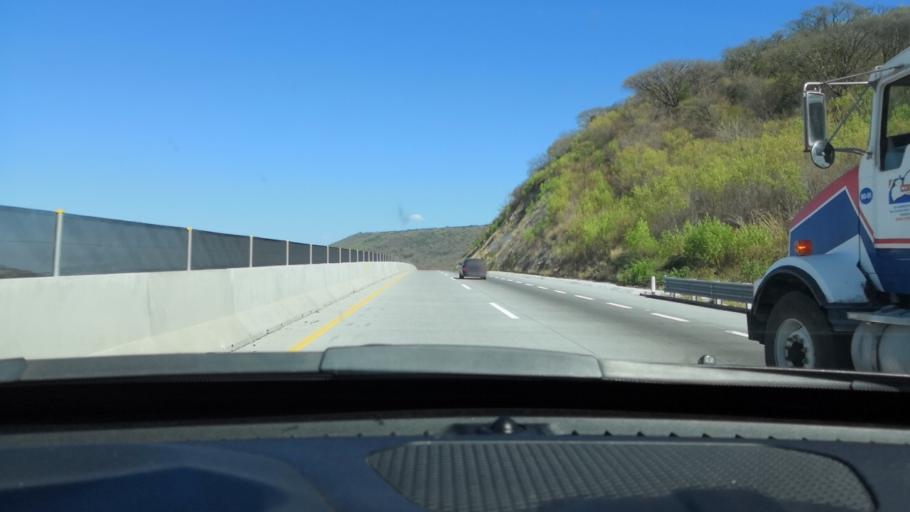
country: MX
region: Jalisco
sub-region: Tlajomulco de Zuniga
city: Galaxia la Noria
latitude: 20.4201
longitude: -103.4567
